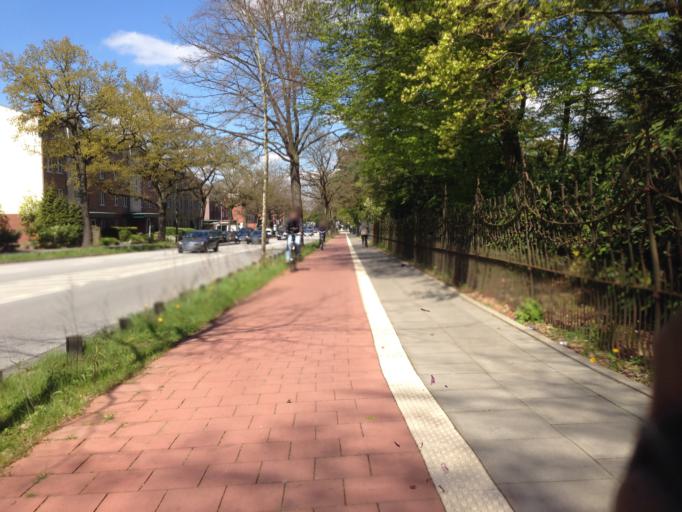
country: DE
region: Hamburg
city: Ohlsdorf
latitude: 53.6172
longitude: 10.0348
